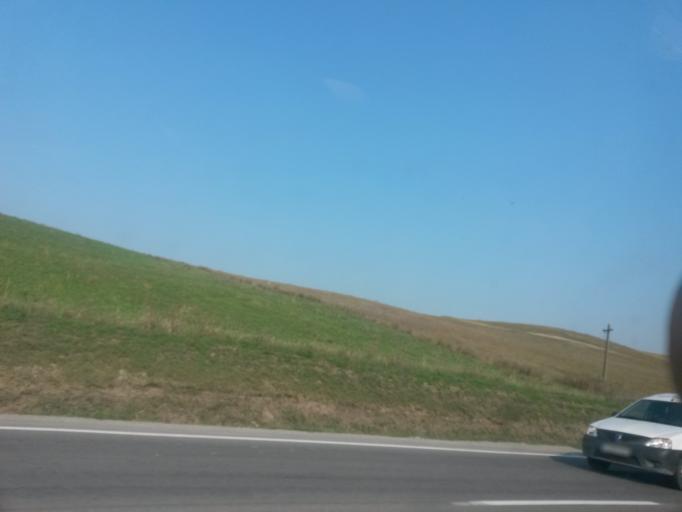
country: RO
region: Cluj
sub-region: Comuna Sandulesti
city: Copaceni
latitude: 46.5893
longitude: 23.7552
